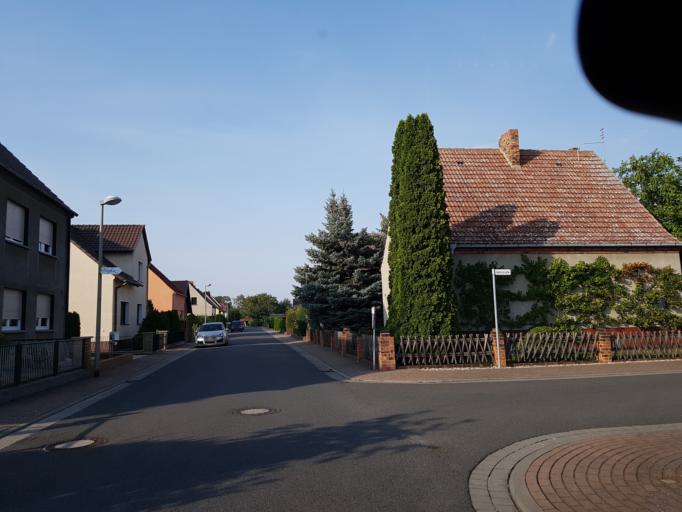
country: DE
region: Saxony-Anhalt
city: Elster
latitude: 51.8322
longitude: 12.8197
